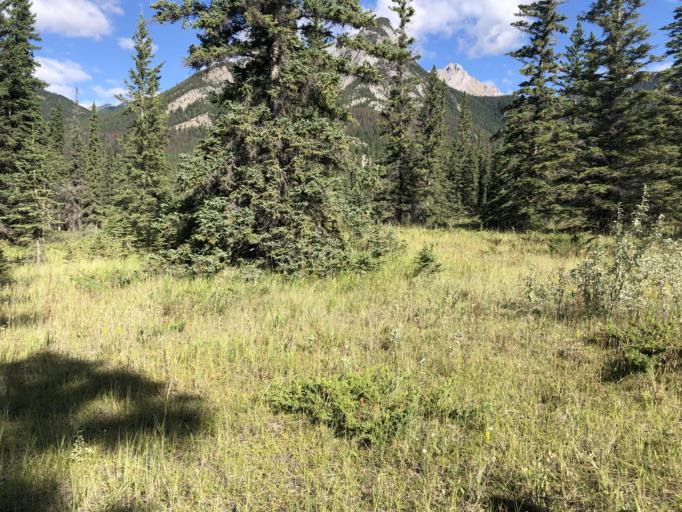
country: CA
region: Alberta
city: Jasper Park Lodge
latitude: 53.0521
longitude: -118.1084
